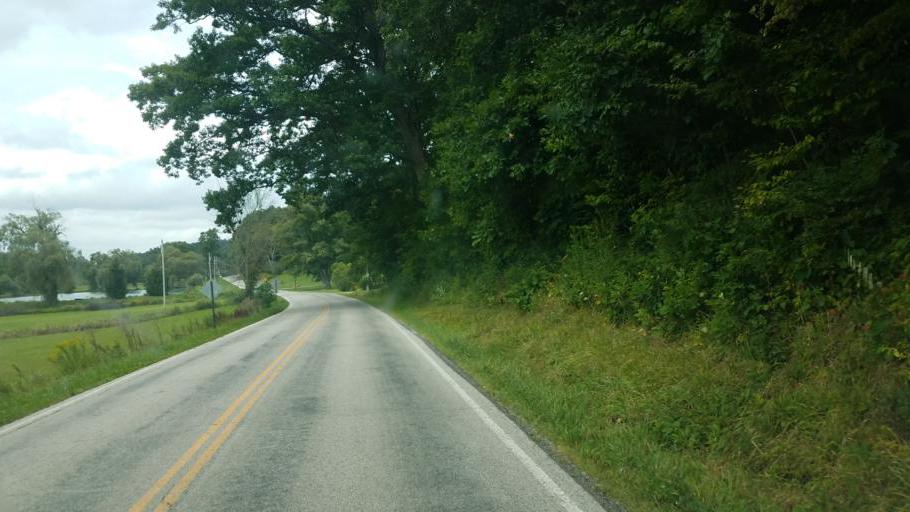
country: US
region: Ohio
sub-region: Sandusky County
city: Bellville
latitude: 40.6639
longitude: -82.4884
